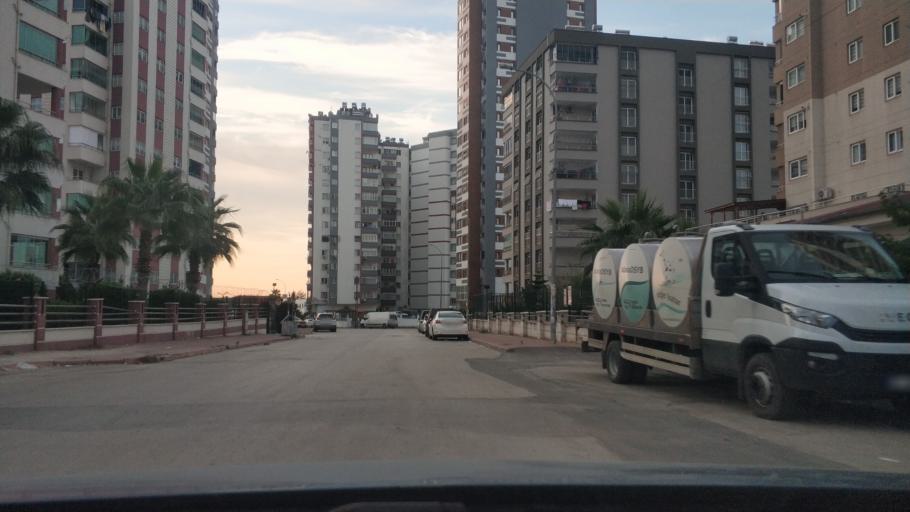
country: TR
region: Adana
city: Seyhan
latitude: 37.0134
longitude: 35.2885
